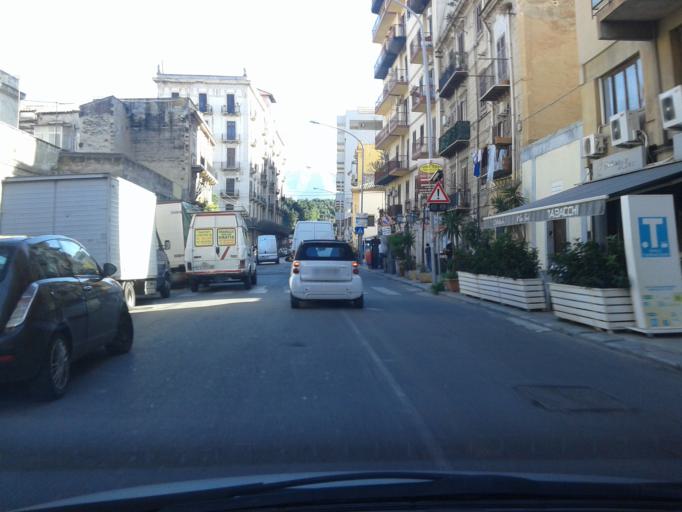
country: IT
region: Sicily
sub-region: Palermo
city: Palermo
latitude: 38.1163
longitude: 13.3509
